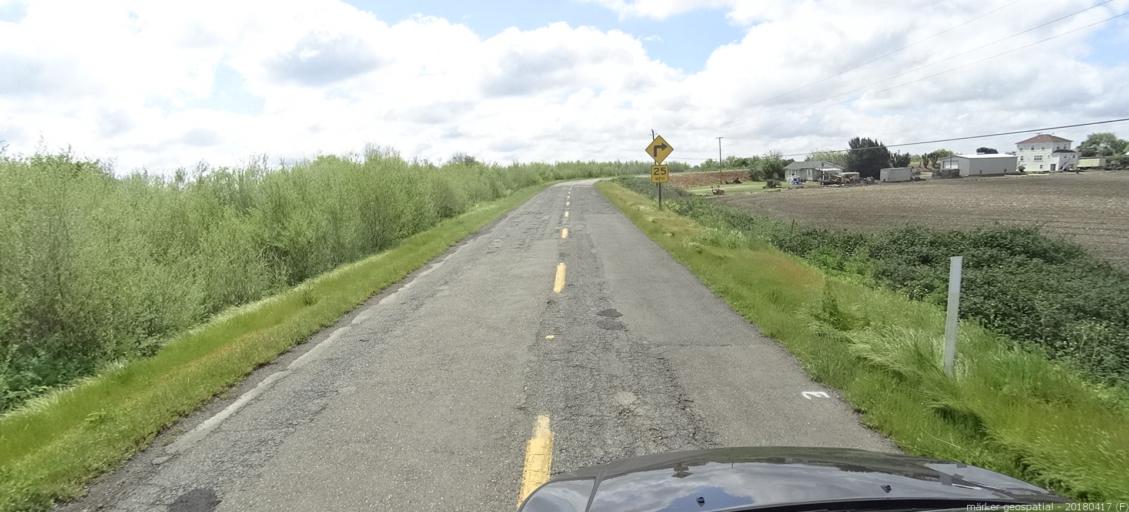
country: US
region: California
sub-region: Sacramento County
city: Walnut Grove
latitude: 38.2036
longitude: -121.5411
